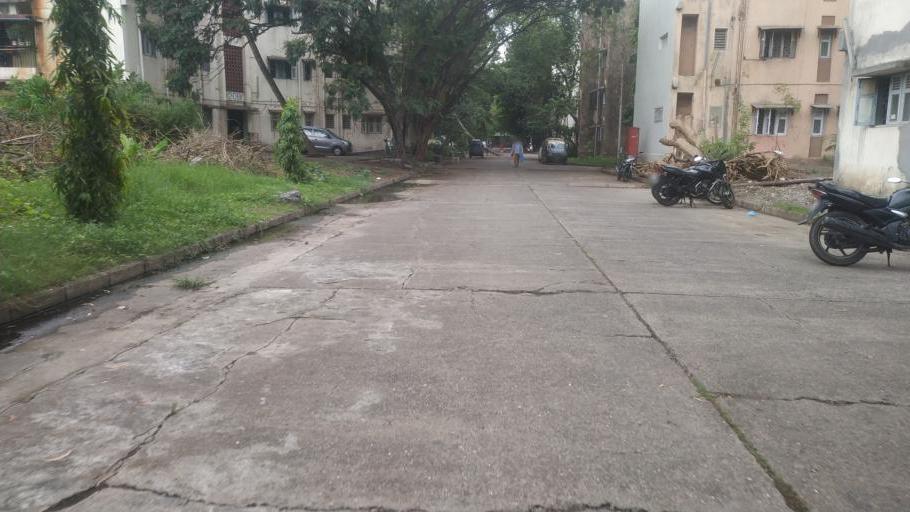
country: IN
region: Maharashtra
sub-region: Mumbai Suburban
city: Mumbai
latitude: 19.0789
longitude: 72.8712
